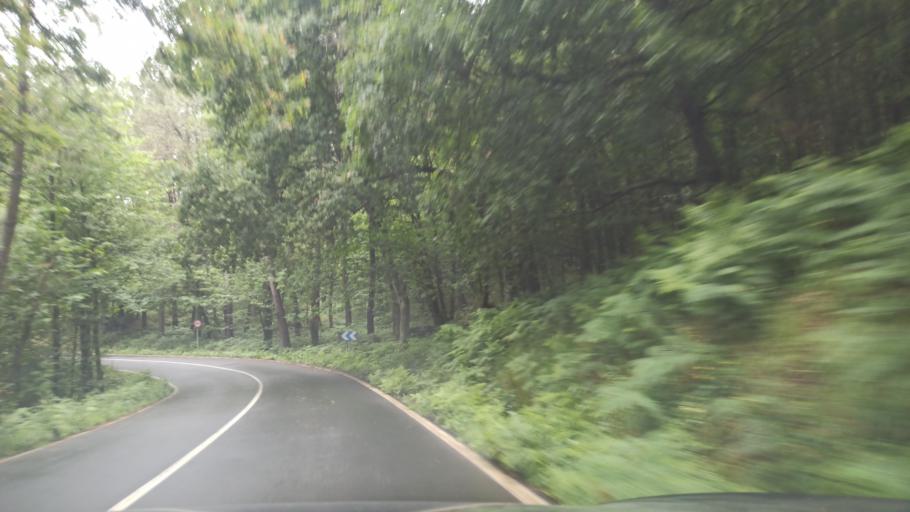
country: ES
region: Galicia
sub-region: Provincia da Coruna
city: Santiso
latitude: 42.7839
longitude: -8.0800
